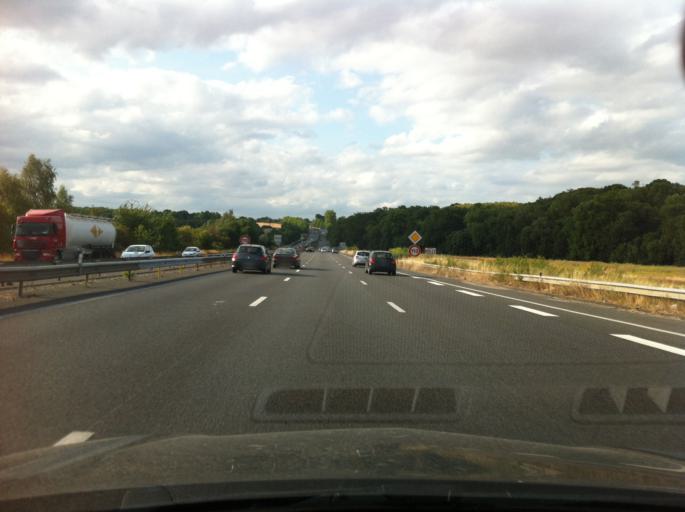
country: FR
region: Ile-de-France
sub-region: Departement de Seine-et-Marne
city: Brie-Comte-Robert
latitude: 48.6665
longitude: 2.6129
